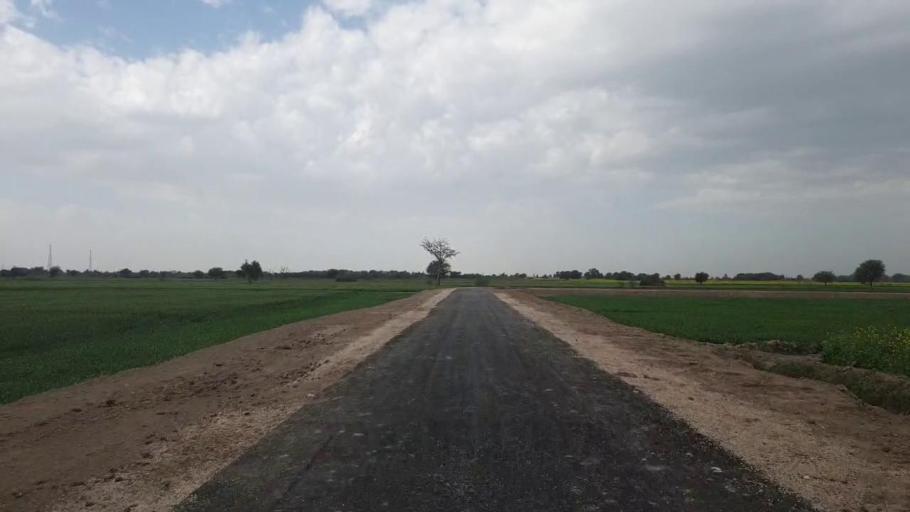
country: PK
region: Sindh
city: Hala
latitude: 25.9747
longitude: 68.4003
